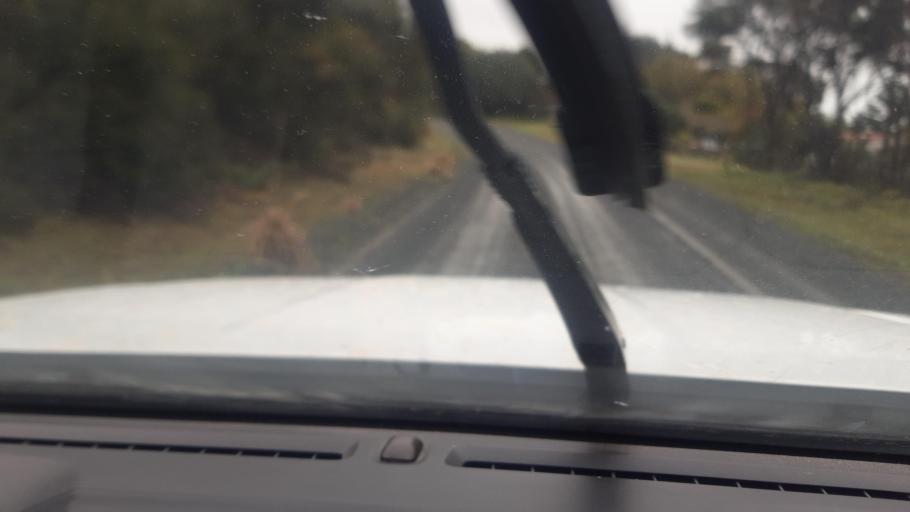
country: NZ
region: Northland
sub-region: Far North District
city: Kaitaia
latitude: -34.9900
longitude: 173.2134
